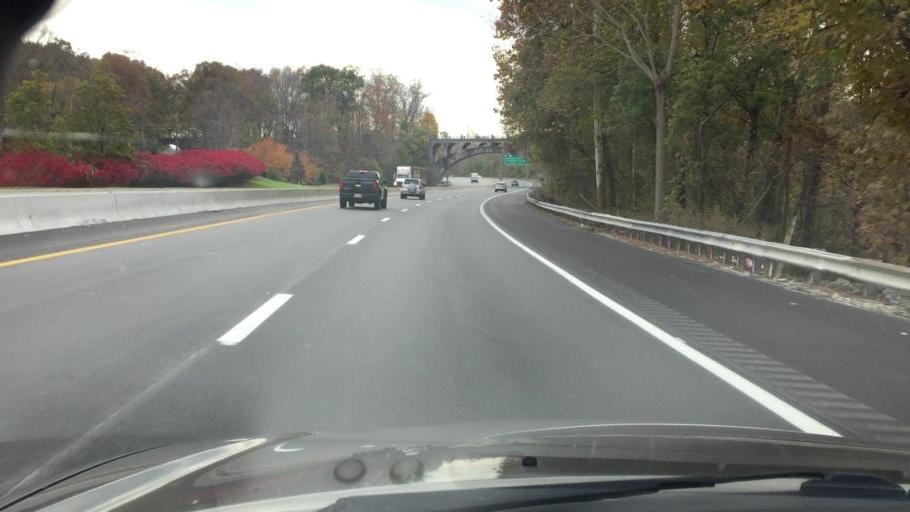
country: US
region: Pennsylvania
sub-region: Monroe County
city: East Stroudsburg
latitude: 40.9392
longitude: -75.1042
